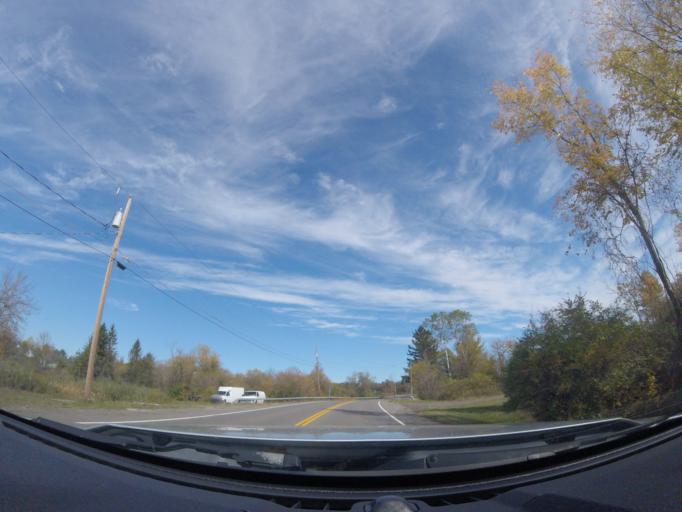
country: US
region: New York
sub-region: Tompkins County
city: Dryden
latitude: 42.5155
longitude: -76.3449
